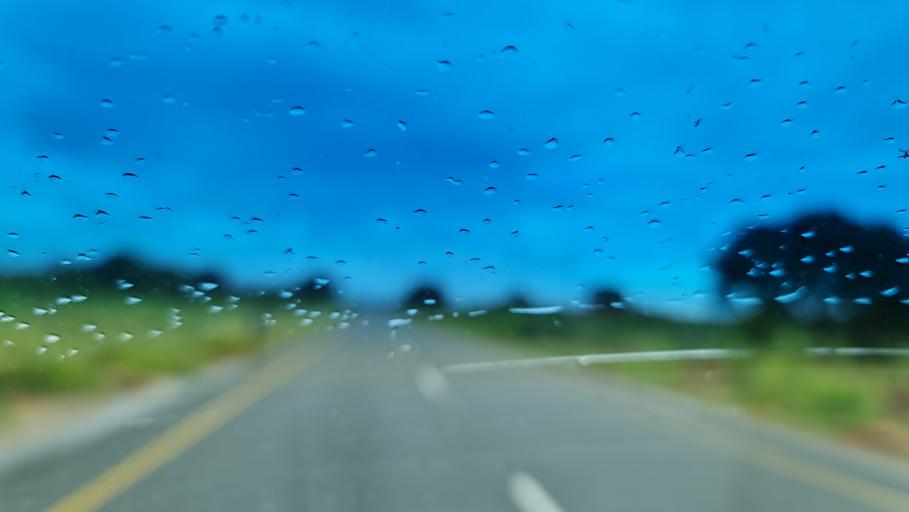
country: MZ
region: Nampula
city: Nampula
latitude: -15.5294
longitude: 39.3318
